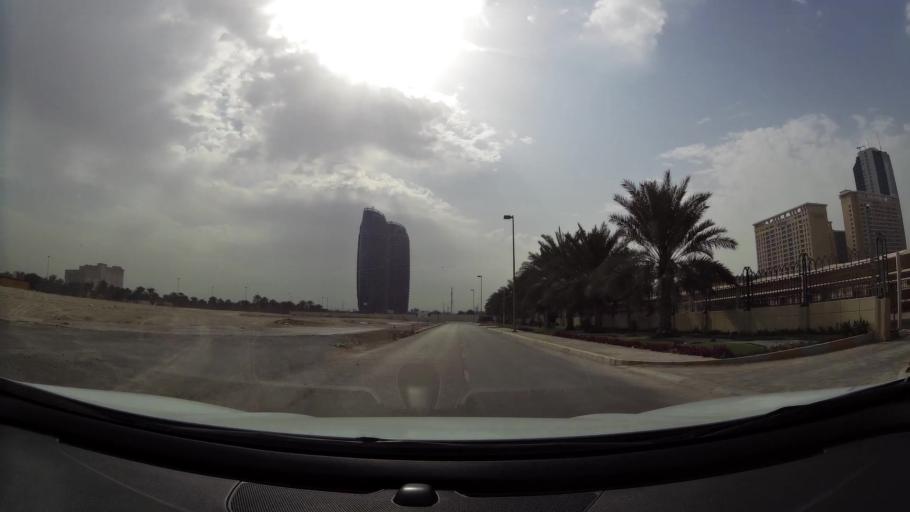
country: AE
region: Abu Dhabi
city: Abu Dhabi
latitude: 24.4595
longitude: 54.3962
